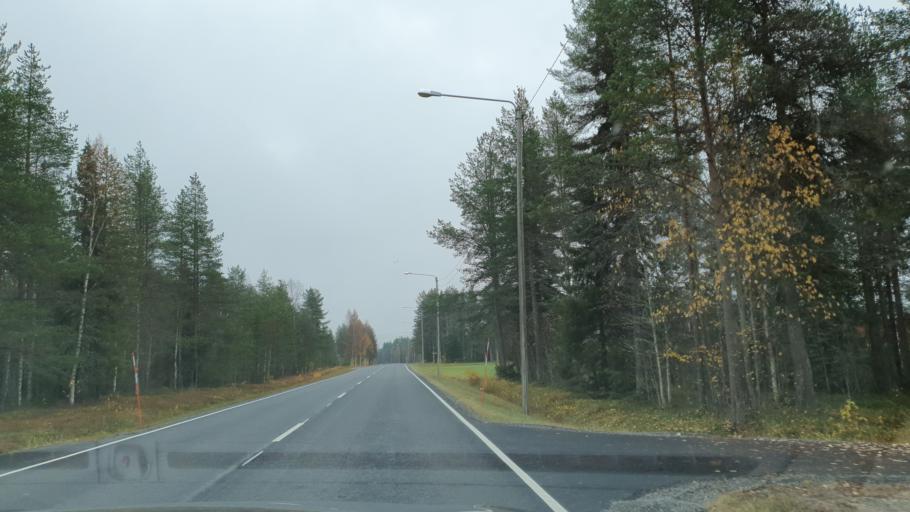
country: FI
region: Lapland
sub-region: Rovaniemi
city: Ranua
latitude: 66.1085
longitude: 26.3213
